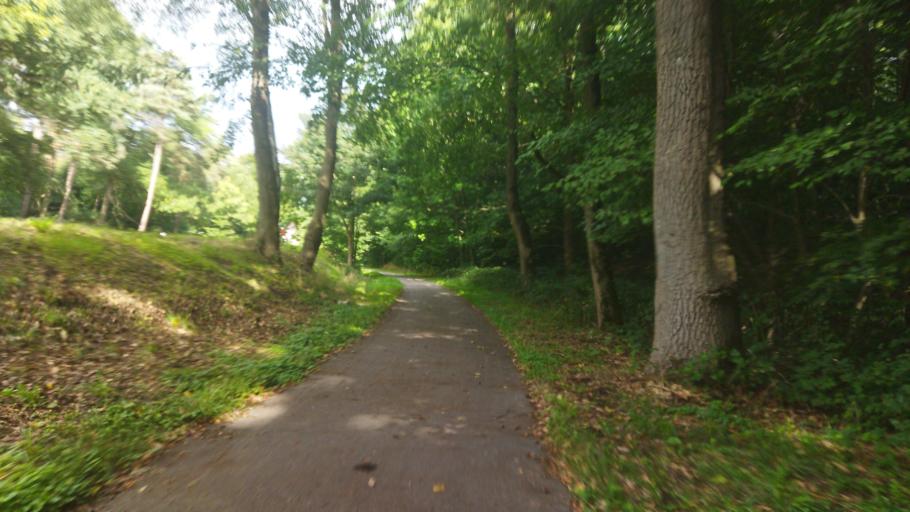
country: DE
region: North Rhine-Westphalia
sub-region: Regierungsbezirk Munster
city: Haltern
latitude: 51.6940
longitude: 7.1898
